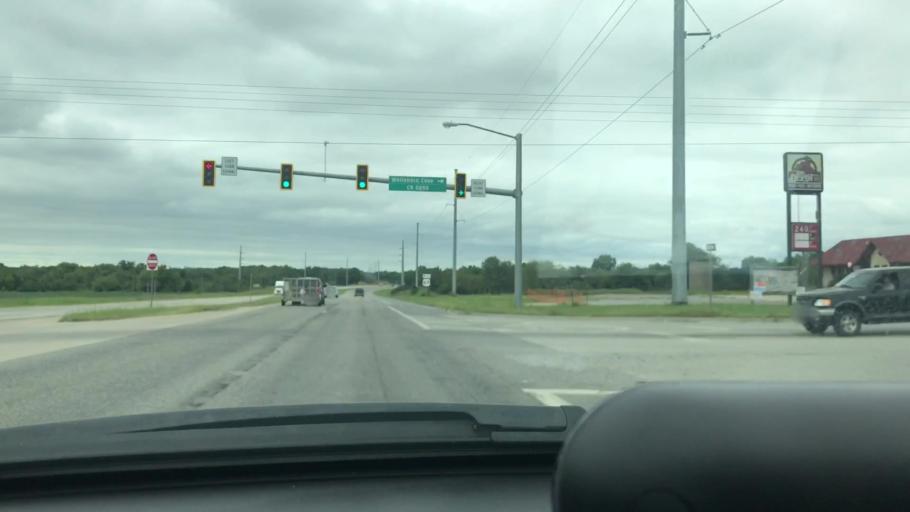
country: US
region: Oklahoma
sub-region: Wagoner County
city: Wagoner
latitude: 36.0171
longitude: -95.3686
